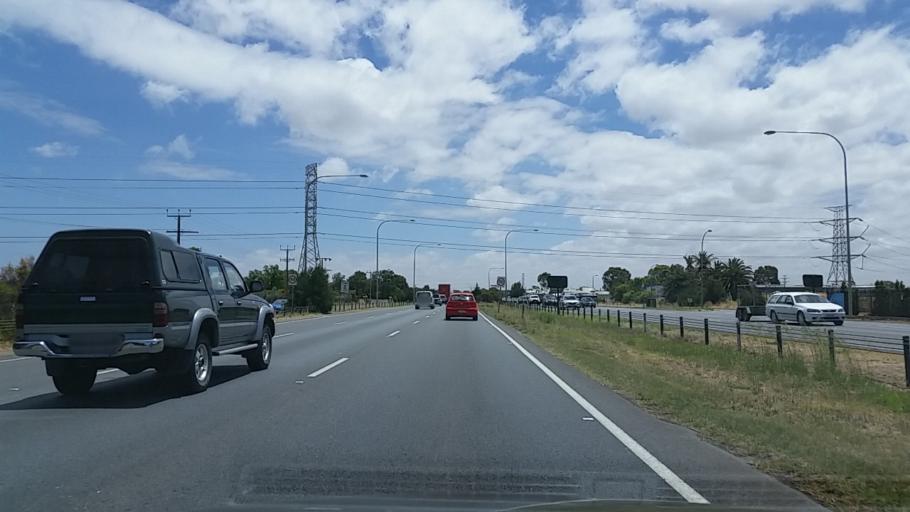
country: AU
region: South Australia
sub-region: Salisbury
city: Salisbury
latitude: -34.7873
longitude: 138.5961
